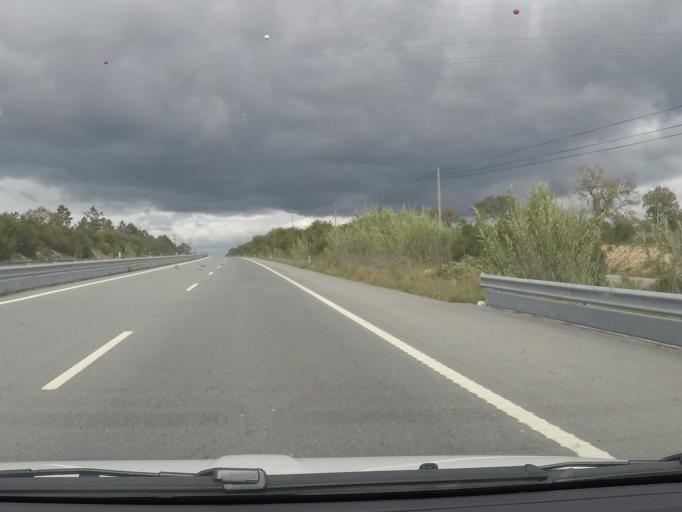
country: PT
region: Setubal
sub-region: Santiago do Cacem
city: Santo Andre
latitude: 37.9898
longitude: -8.7712
